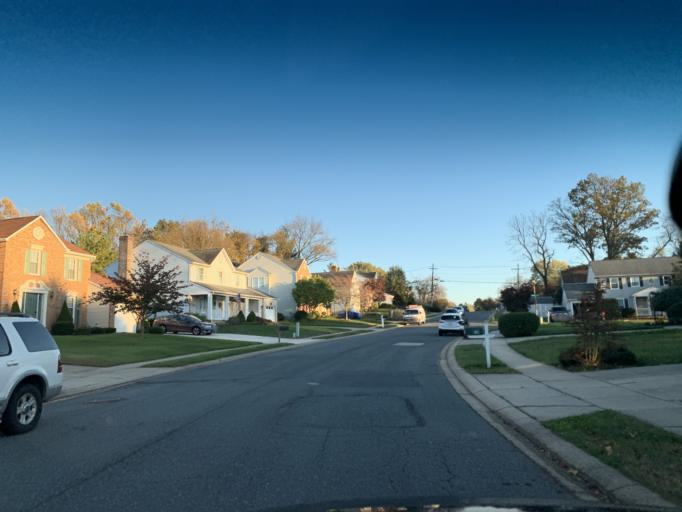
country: US
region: Maryland
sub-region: Harford County
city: Bel Air North
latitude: 39.5604
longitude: -76.3781
